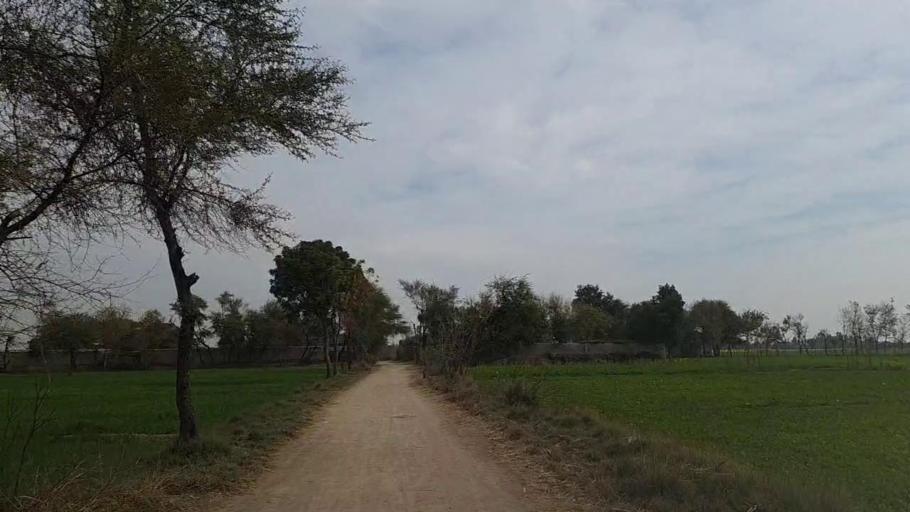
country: PK
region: Sindh
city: Nawabshah
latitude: 26.3841
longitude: 68.4455
